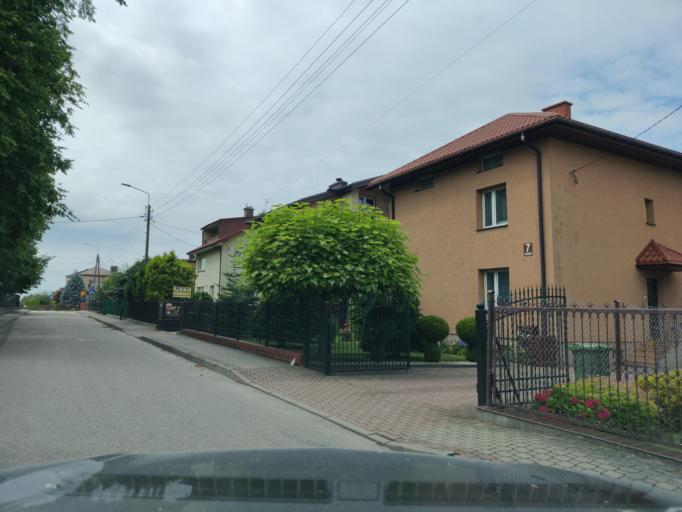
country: PL
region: Podlasie
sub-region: Powiat zambrowski
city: Zambrow
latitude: 52.9906
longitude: 22.2417
